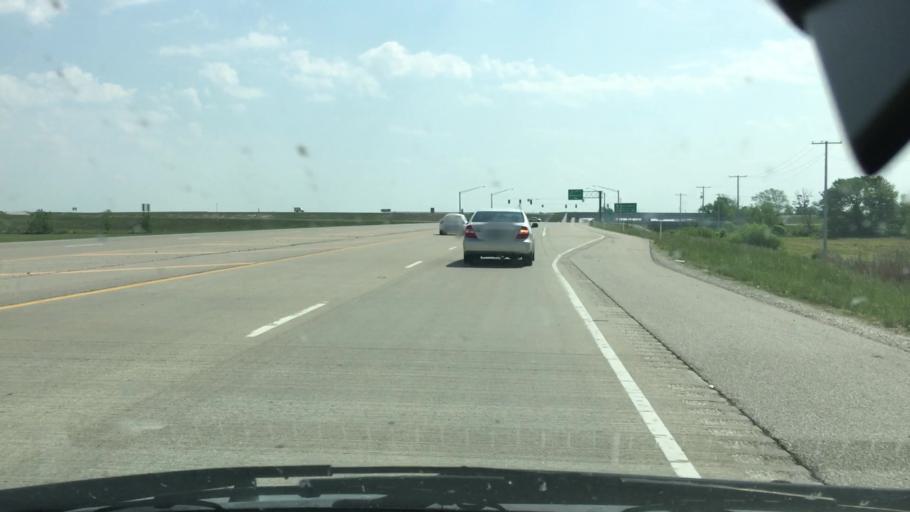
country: US
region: Indiana
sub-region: Daviess County
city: Washington
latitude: 38.6550
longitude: -87.1266
